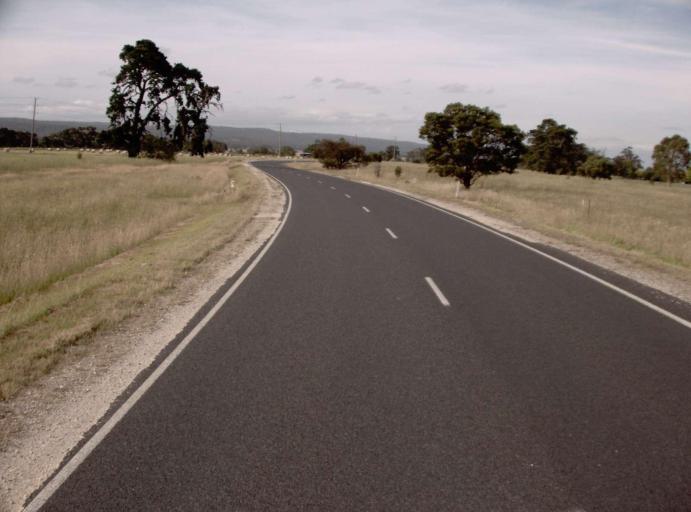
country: AU
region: Victoria
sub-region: Latrobe
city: Traralgon
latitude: -38.1049
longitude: 146.5930
